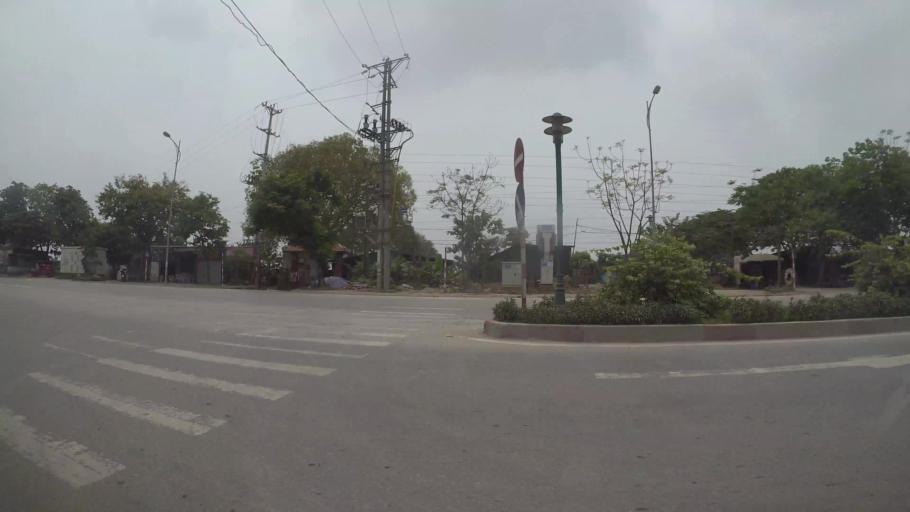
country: VN
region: Ha Noi
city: Ha Dong
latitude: 20.9905
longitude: 105.7368
